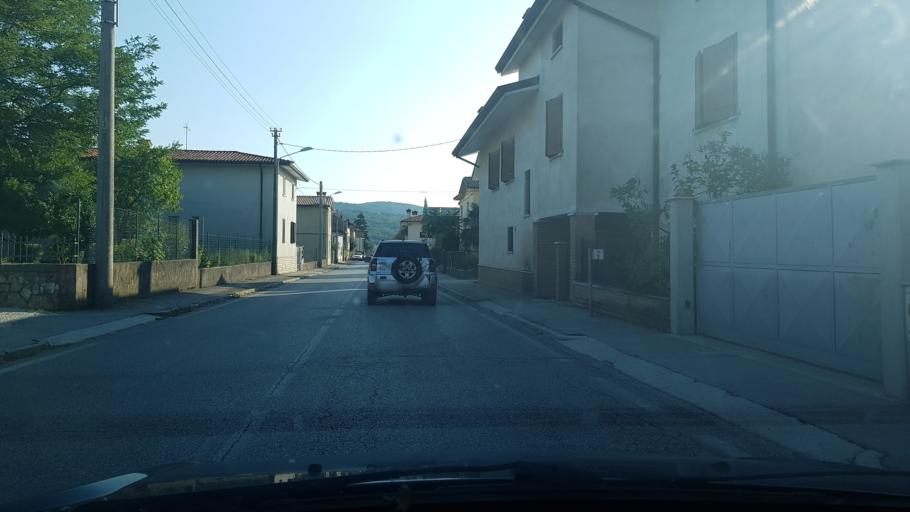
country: IT
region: Friuli Venezia Giulia
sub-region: Provincia di Gorizia
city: Savogna d'Isonzo
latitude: 45.9081
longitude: 13.5779
